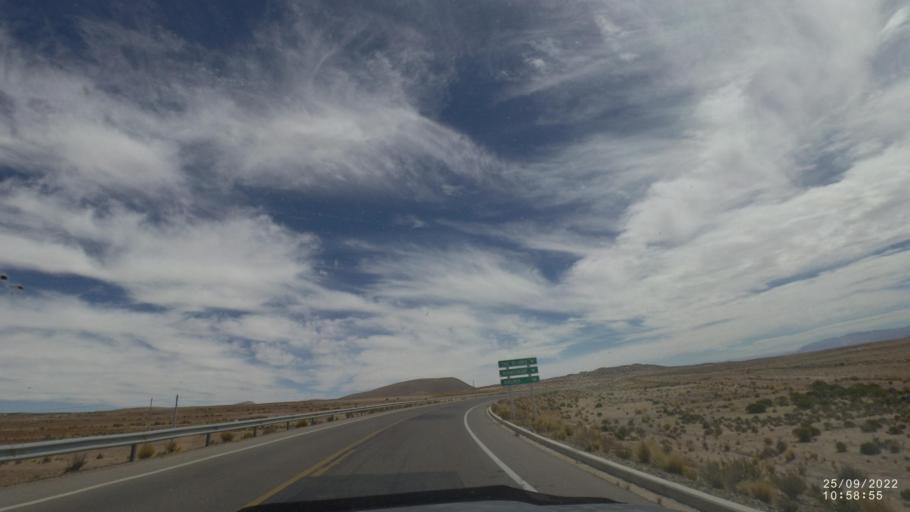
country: BO
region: Oruro
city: Challapata
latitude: -19.4571
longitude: -66.9093
